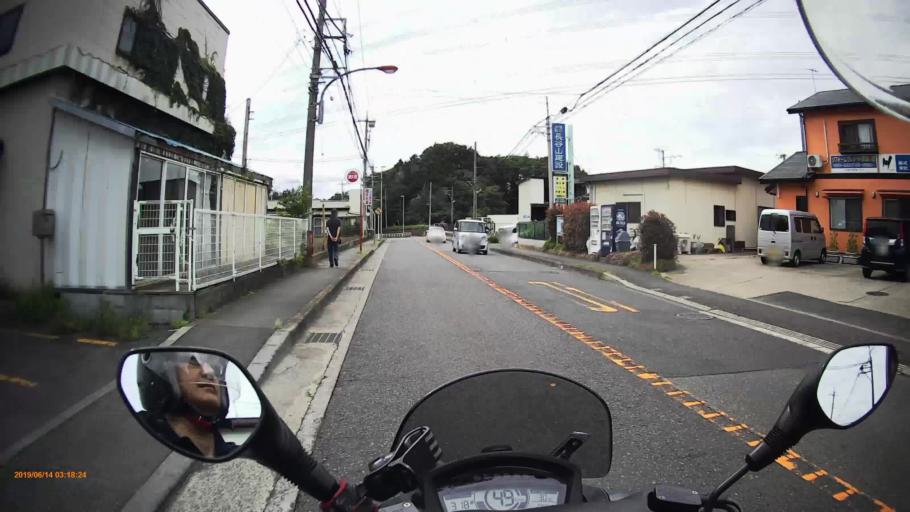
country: JP
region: Kanagawa
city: Minami-rinkan
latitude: 35.4189
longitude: 139.4561
